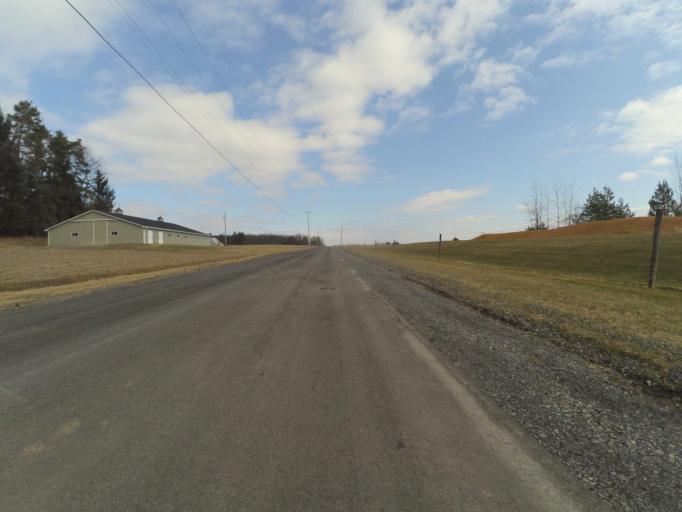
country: US
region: Pennsylvania
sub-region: Centre County
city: Park Forest Village
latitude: 40.7676
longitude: -77.9255
